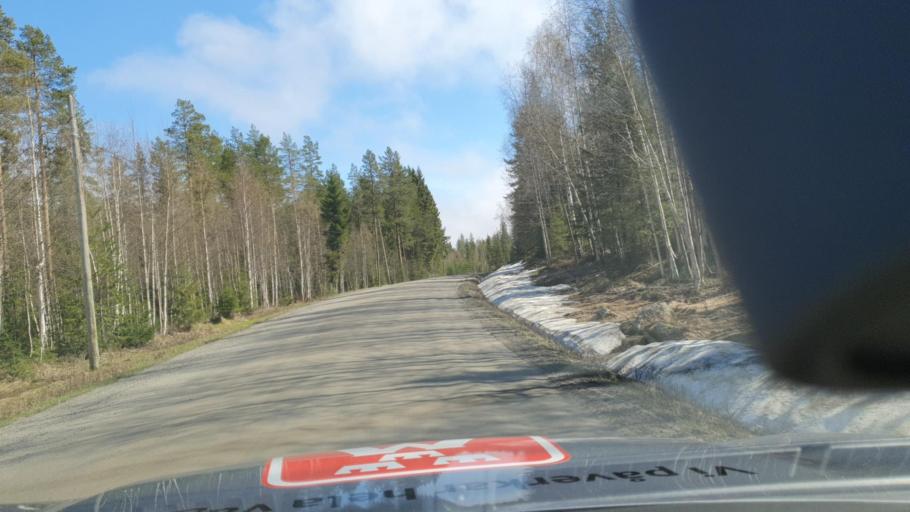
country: SE
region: Vaesterbotten
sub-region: Bjurholms Kommun
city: Bjurholm
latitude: 63.6847
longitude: 18.9711
